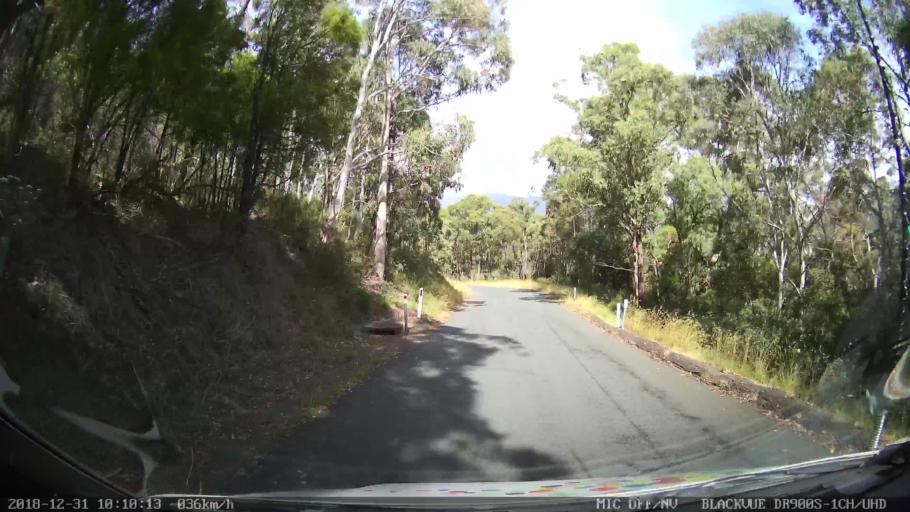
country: AU
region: New South Wales
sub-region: Snowy River
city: Jindabyne
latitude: -36.5360
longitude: 148.1713
